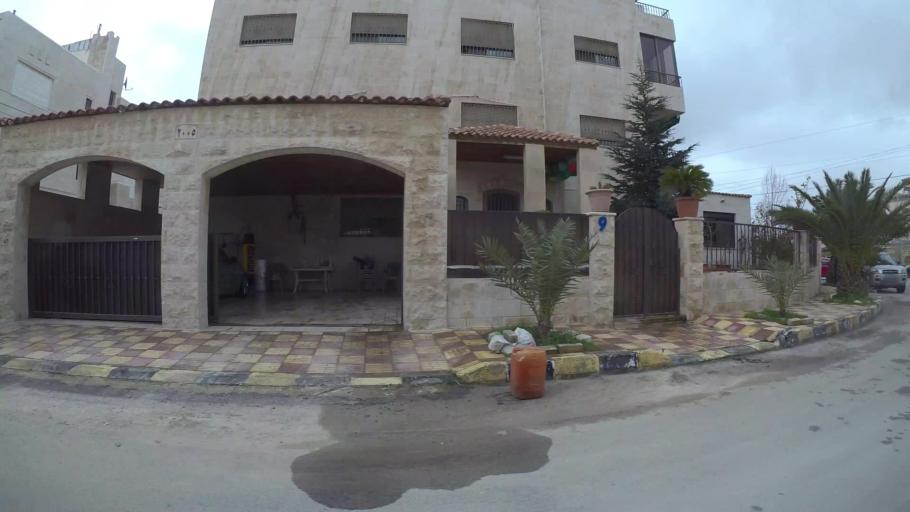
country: JO
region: Amman
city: Al Jubayhah
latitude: 31.9922
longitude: 35.8385
